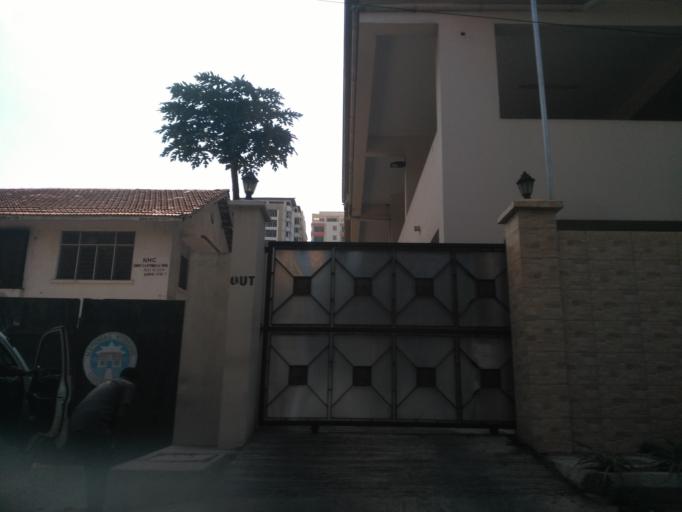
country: TZ
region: Dar es Salaam
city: Dar es Salaam
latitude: -6.8055
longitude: 39.2840
